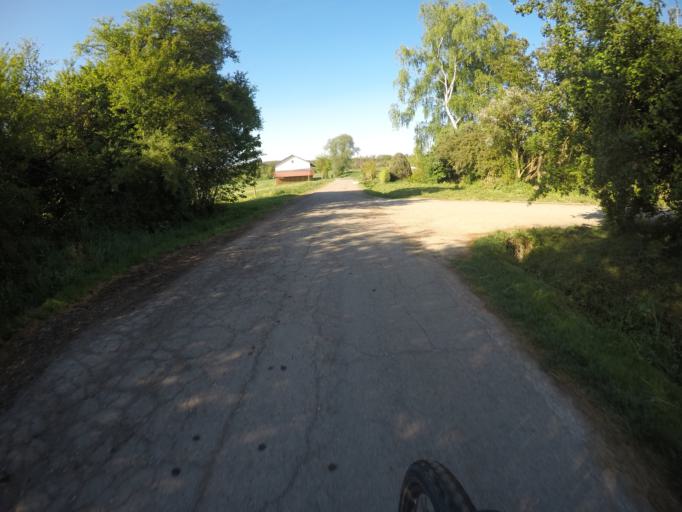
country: DE
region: Baden-Wuerttemberg
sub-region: Regierungsbezirk Stuttgart
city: Wolfschlugen
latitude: 48.6375
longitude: 9.2657
